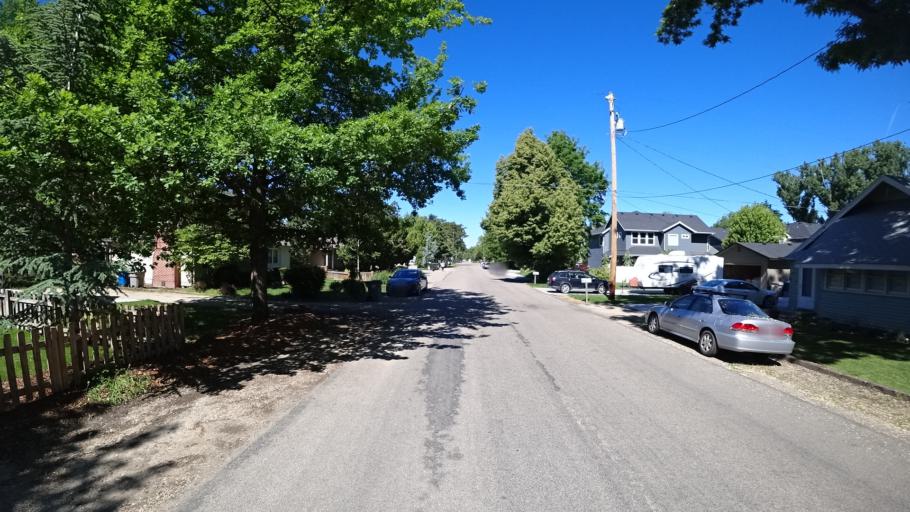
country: US
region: Idaho
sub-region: Ada County
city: Garden City
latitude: 43.6426
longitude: -116.2215
